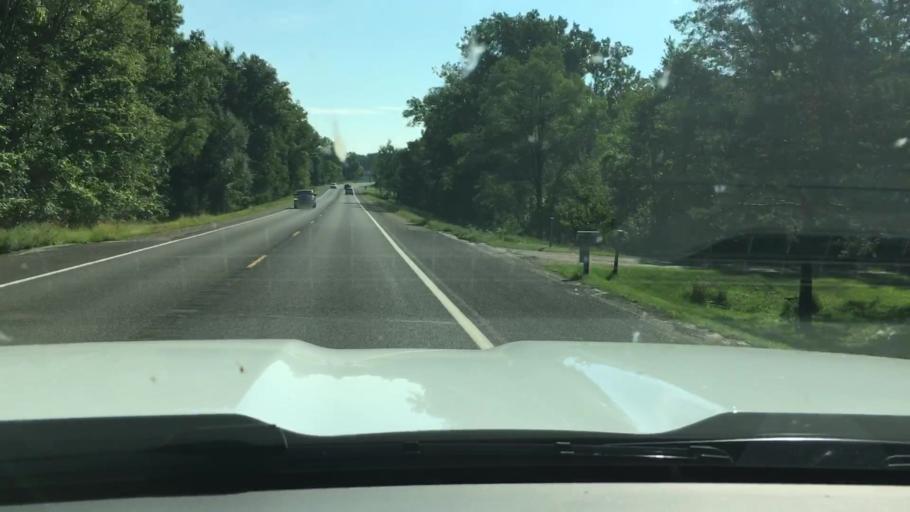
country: US
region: Michigan
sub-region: Montcalm County
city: Edmore
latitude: 43.4080
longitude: -84.9893
